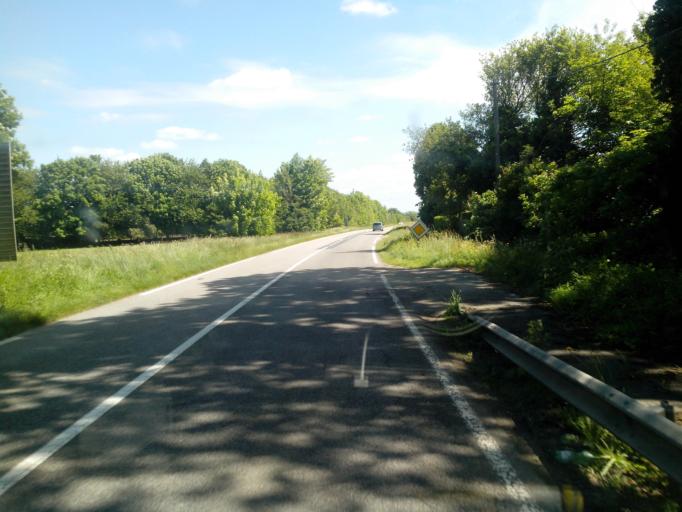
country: FR
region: Haute-Normandie
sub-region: Departement de la Seine-Maritime
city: Tancarville
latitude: 49.4963
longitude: 0.4363
